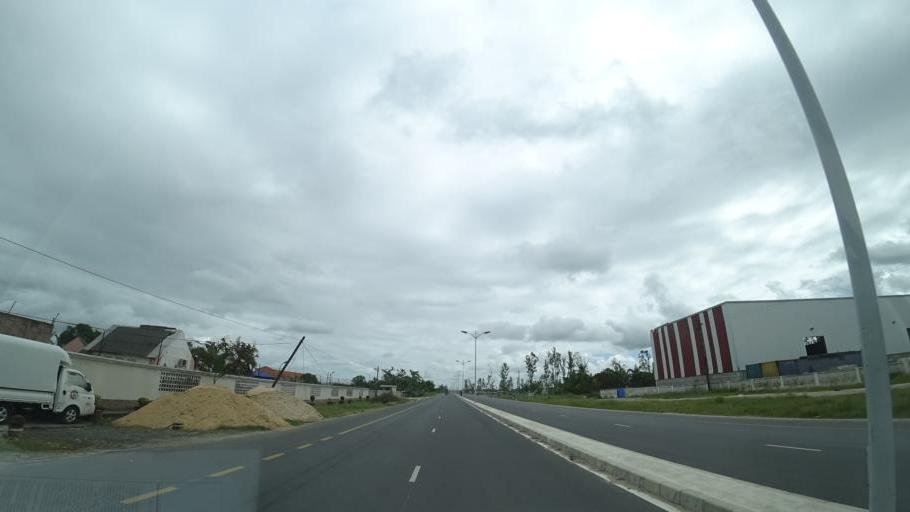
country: MZ
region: Sofala
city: Dondo
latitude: -19.7053
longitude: 34.7910
